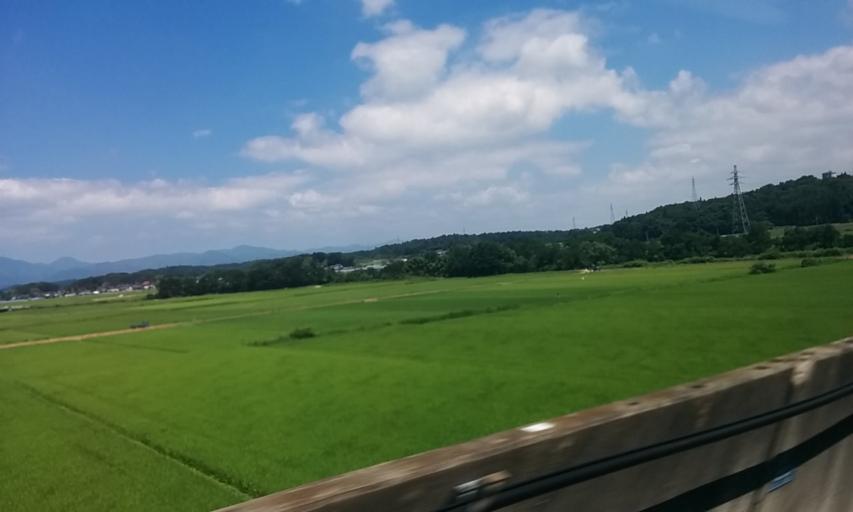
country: JP
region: Fukushima
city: Sukagawa
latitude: 37.2588
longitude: 140.3084
